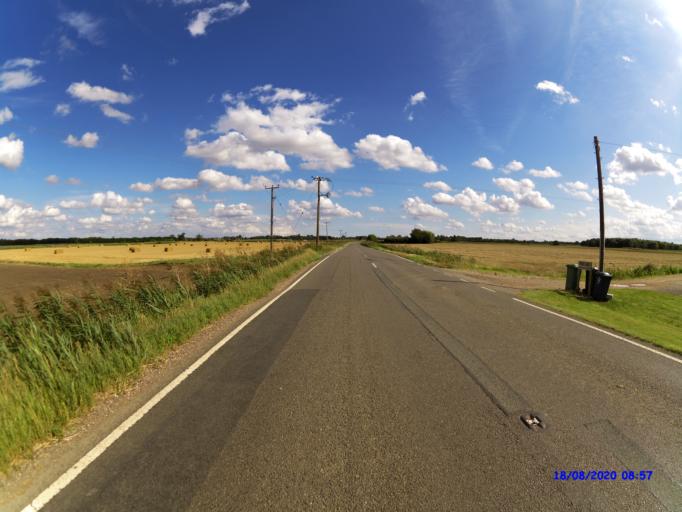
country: GB
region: England
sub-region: Cambridgeshire
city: Ramsey
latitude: 52.4782
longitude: -0.0998
